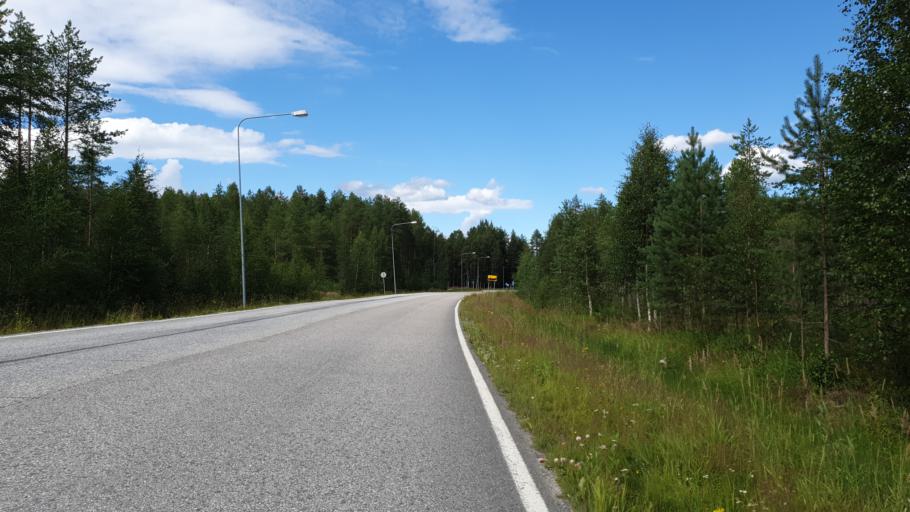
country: FI
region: Kainuu
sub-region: Kehys-Kainuu
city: Kuhmo
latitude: 64.1167
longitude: 29.5269
